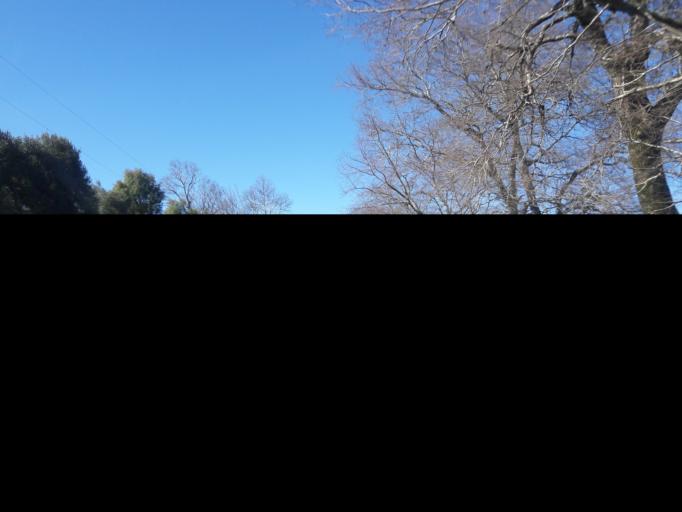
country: CL
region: Araucania
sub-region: Provincia de Malleco
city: Victoria
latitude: -38.2696
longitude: -72.2117
